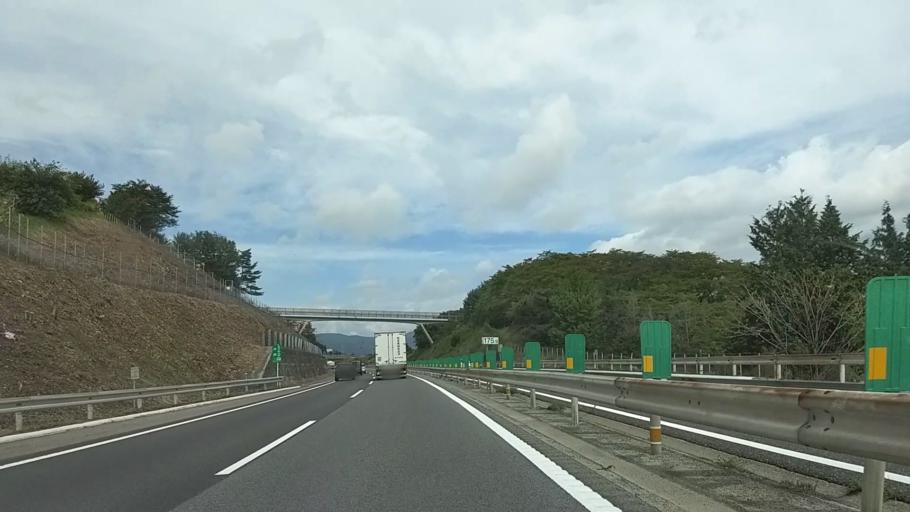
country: JP
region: Nagano
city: Suwa
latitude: 36.0126
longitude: 138.0895
